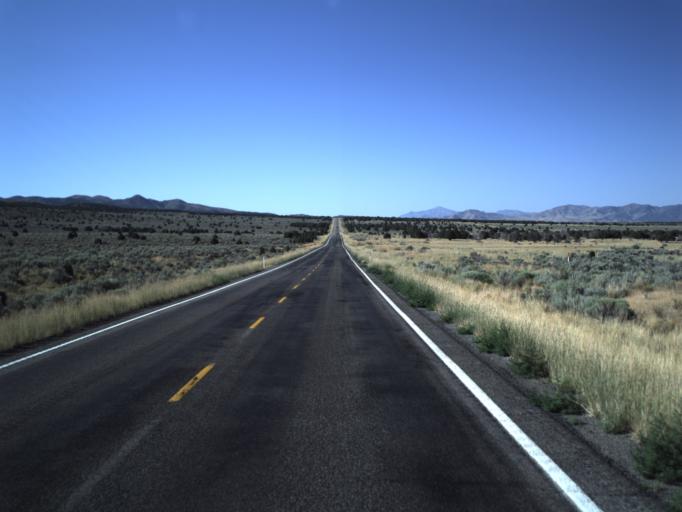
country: US
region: Utah
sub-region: Juab County
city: Mona
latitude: 39.8640
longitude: -112.1381
